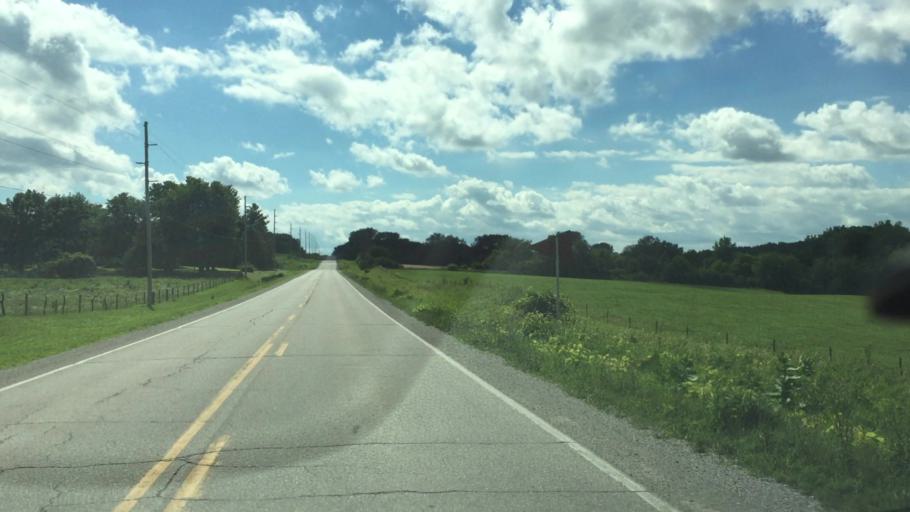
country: US
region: Iowa
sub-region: Linn County
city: Ely
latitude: 41.8474
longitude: -91.5944
